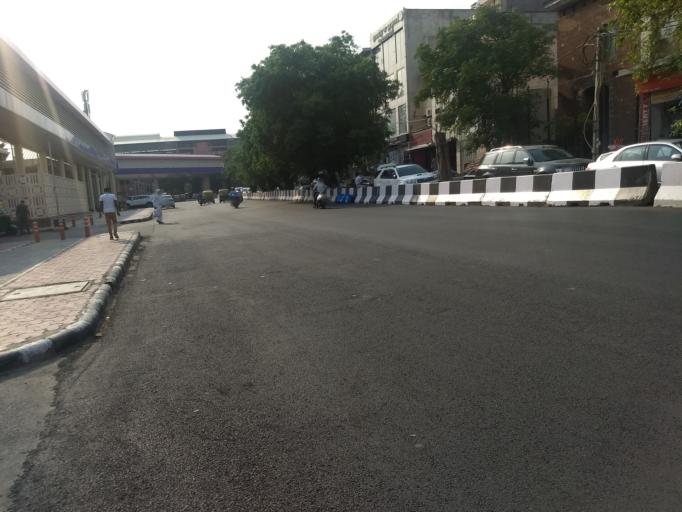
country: IN
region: NCT
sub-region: New Delhi
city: New Delhi
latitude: 28.5697
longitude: 77.2382
